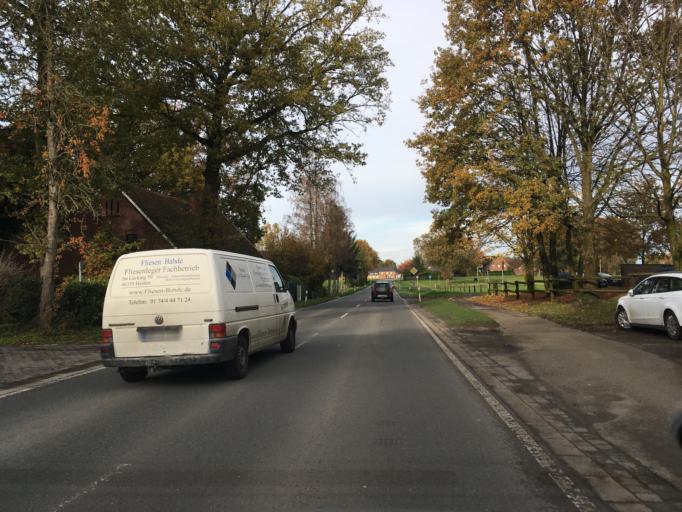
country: DE
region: North Rhine-Westphalia
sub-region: Regierungsbezirk Munster
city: Heiden
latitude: 51.7986
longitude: 6.9543
